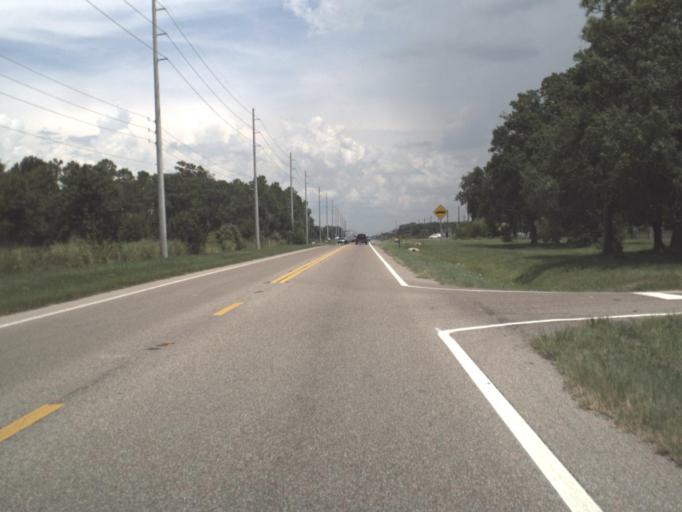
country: US
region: Florida
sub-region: Hillsborough County
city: Sun City Center
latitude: 27.7591
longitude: -82.3351
